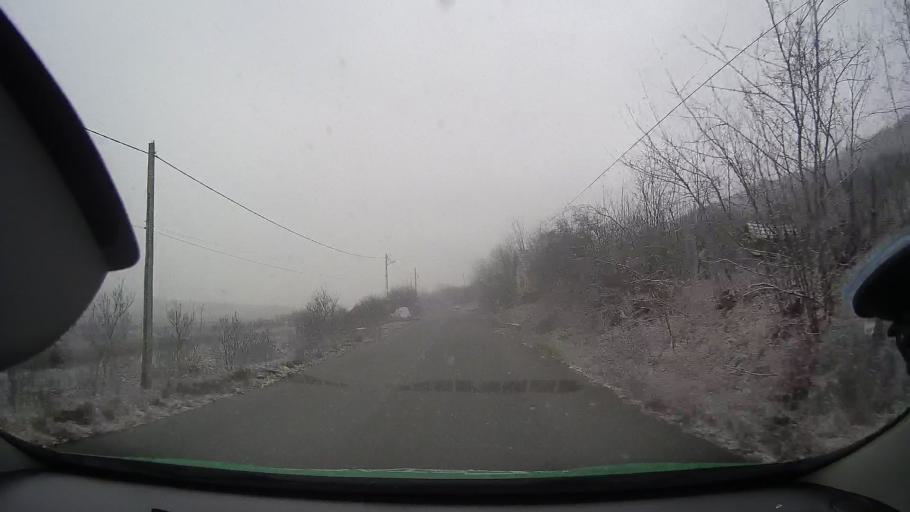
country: RO
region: Alba
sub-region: Comuna Noslac
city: Noslac
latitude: 46.3535
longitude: 23.9329
